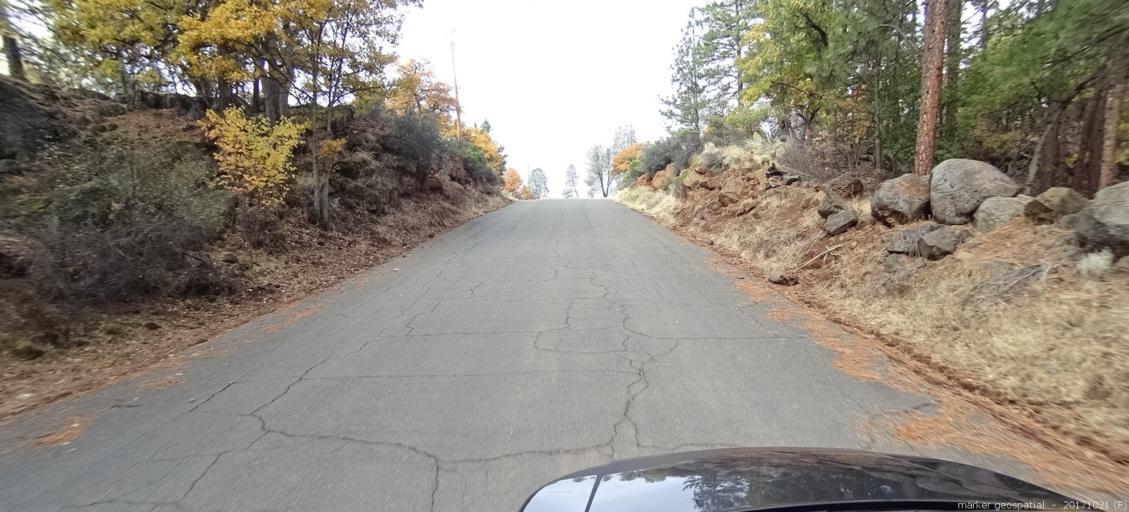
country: US
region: California
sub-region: Shasta County
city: Burney
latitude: 40.9149
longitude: -121.5590
